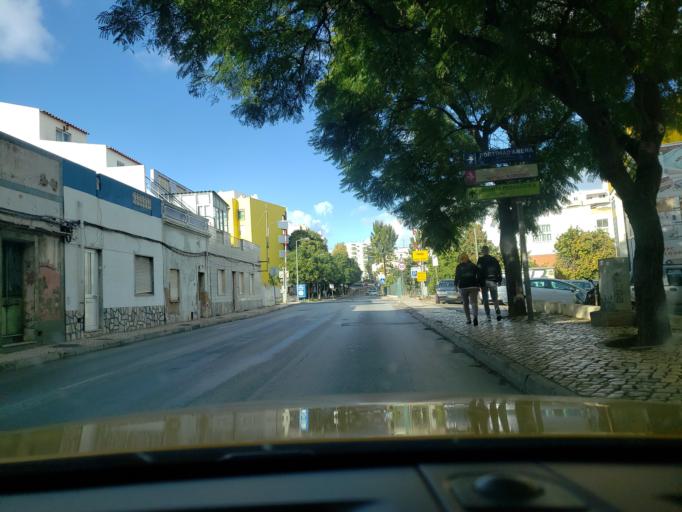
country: PT
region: Faro
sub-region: Portimao
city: Portimao
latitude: 37.1449
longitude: -8.5405
